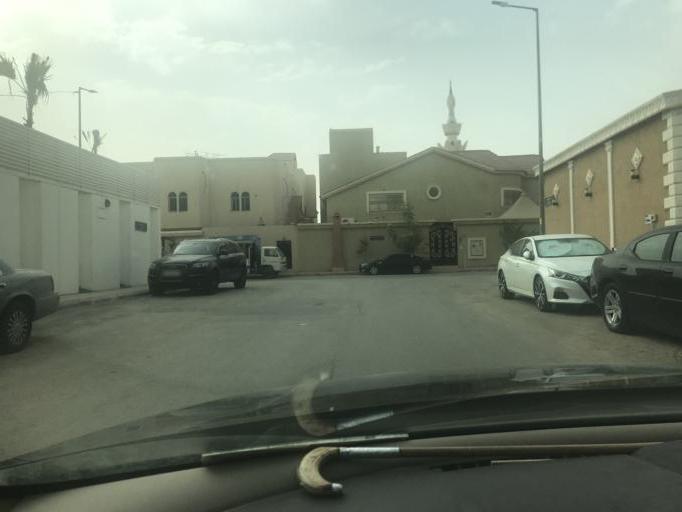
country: SA
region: Ar Riyad
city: Riyadh
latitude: 24.7328
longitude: 46.7886
